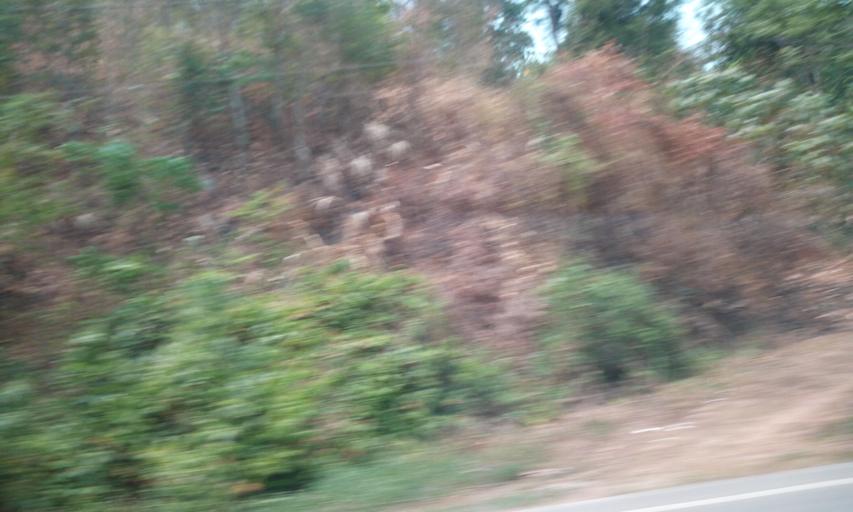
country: TH
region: Chiang Rai
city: Pa Daet
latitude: 19.6151
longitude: 100.0072
